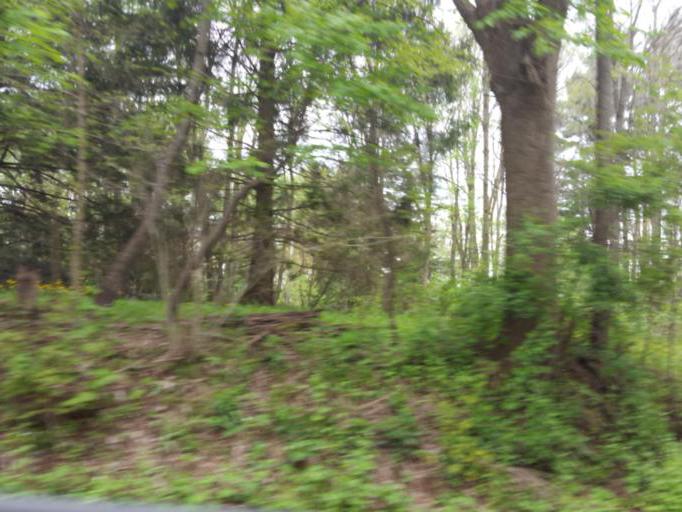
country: US
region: Ohio
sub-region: Richland County
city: Lexington
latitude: 40.6593
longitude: -82.6464
